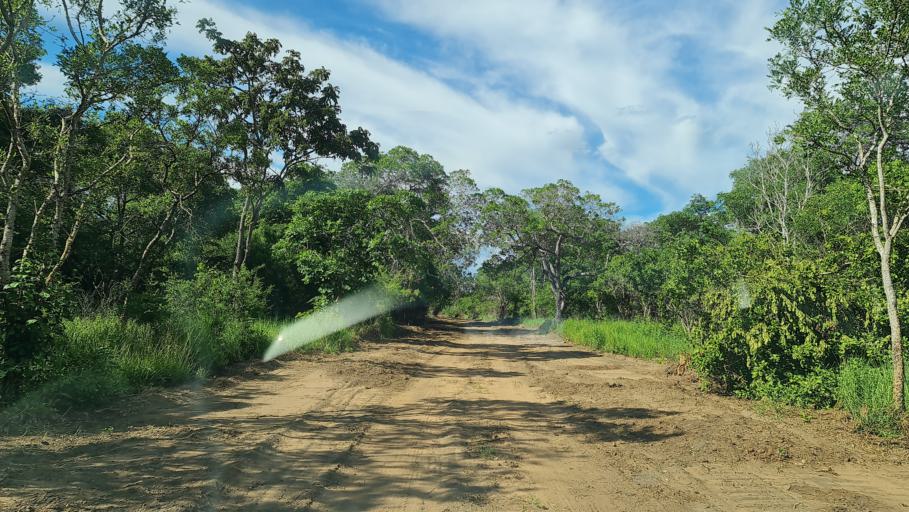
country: MZ
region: Nampula
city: Antonio Enes
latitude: -15.5221
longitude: 40.1280
